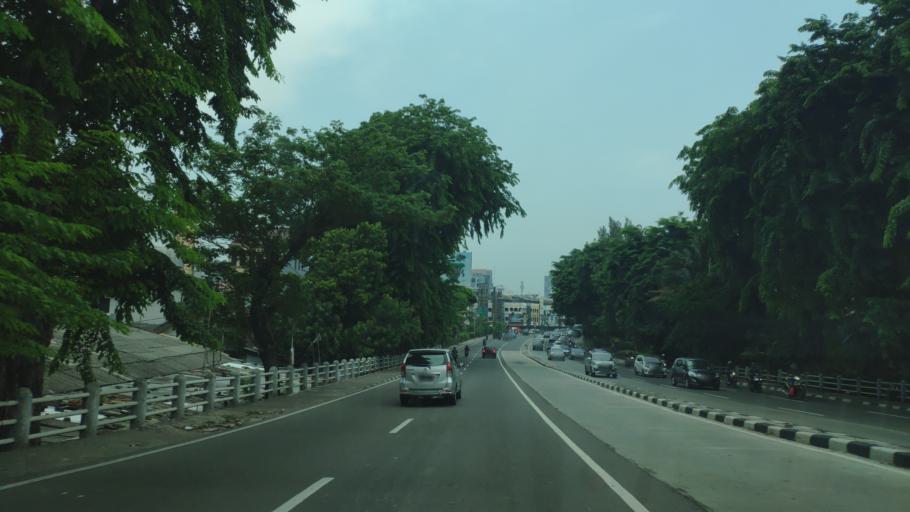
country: ID
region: Jakarta Raya
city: Jakarta
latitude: -6.1726
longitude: 106.8067
